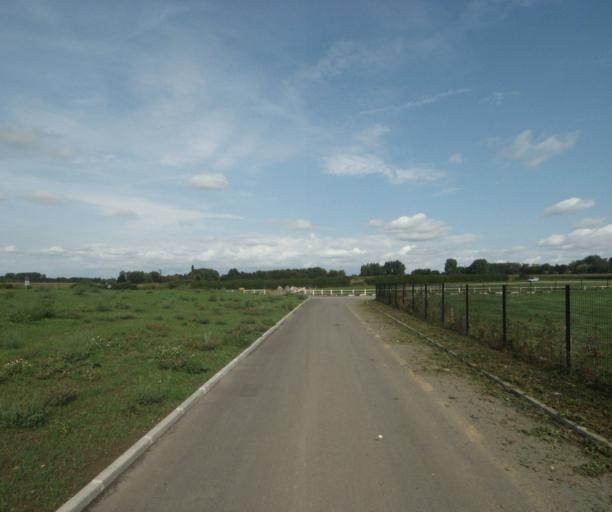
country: FR
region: Nord-Pas-de-Calais
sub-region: Departement du Nord
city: Bondues
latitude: 50.6870
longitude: 3.0842
